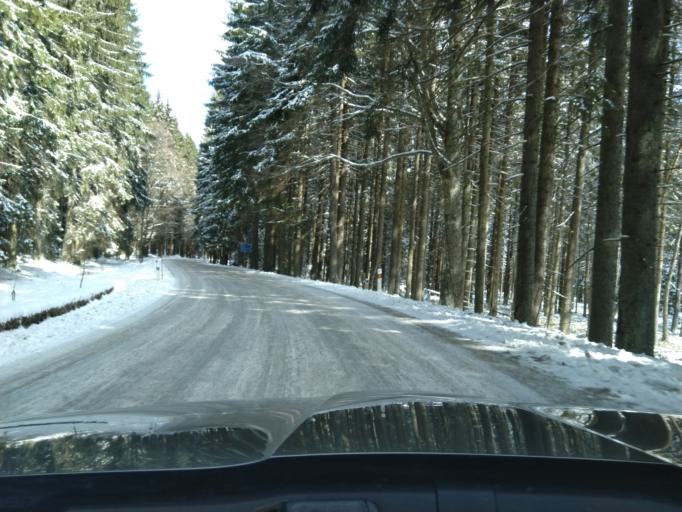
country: CZ
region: Jihocesky
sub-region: Okres Prachatice
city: Stachy
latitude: 49.0554
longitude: 13.6560
